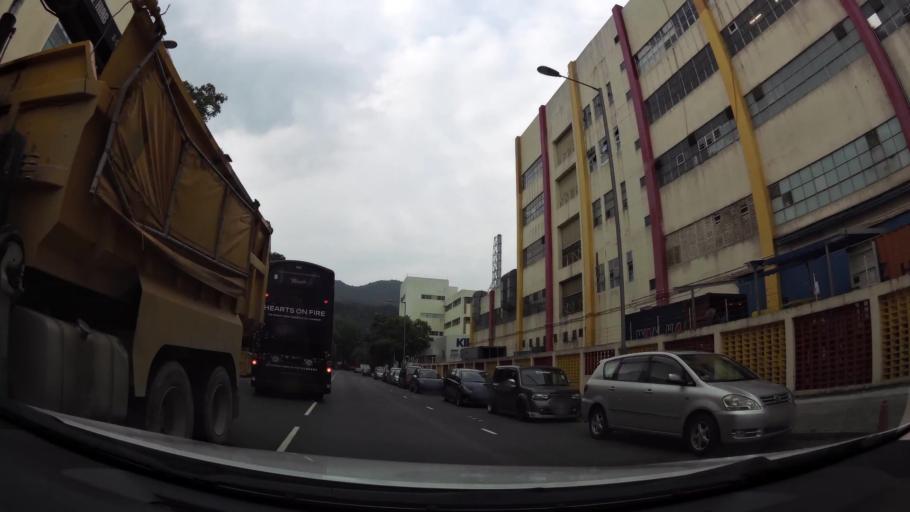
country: HK
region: Tai Po
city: Tai Po
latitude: 22.4596
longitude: 114.1848
